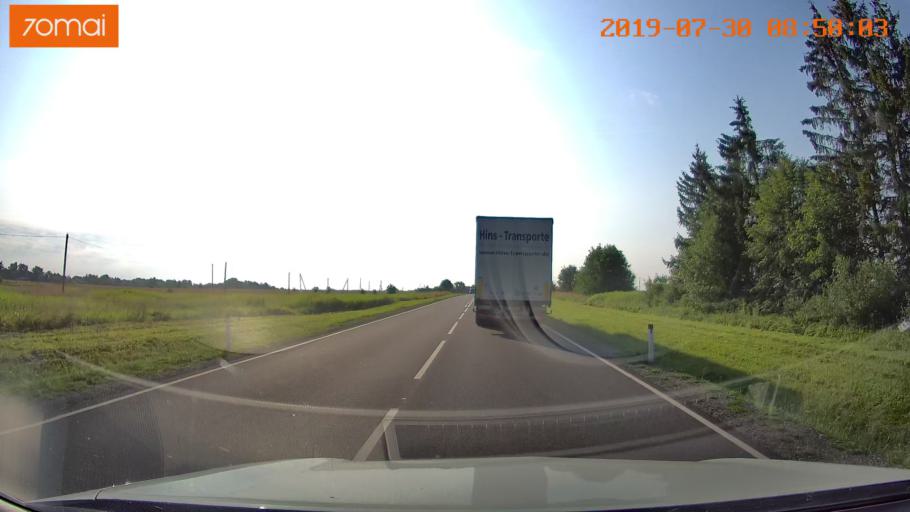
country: RU
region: Kaliningrad
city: Chernyakhovsk
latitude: 54.6095
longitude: 21.9329
